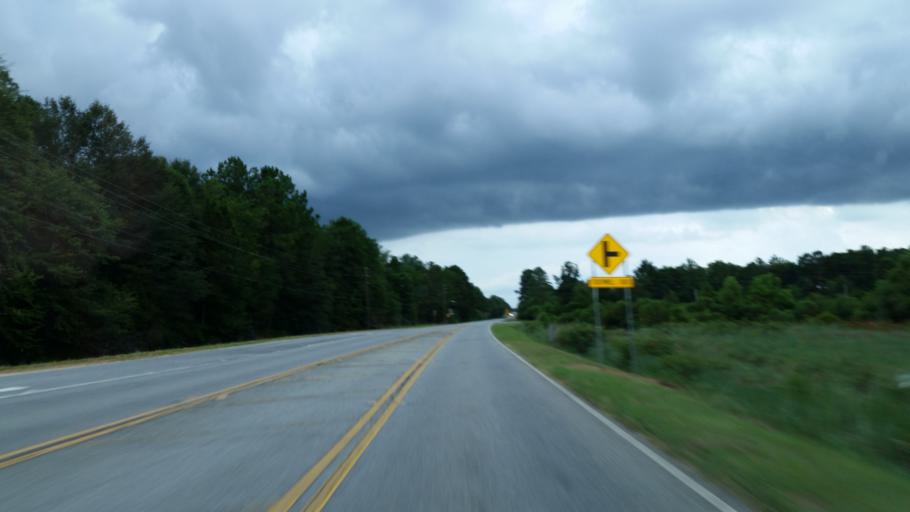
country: US
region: Georgia
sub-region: Tift County
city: Unionville
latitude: 31.4158
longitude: -83.4818
